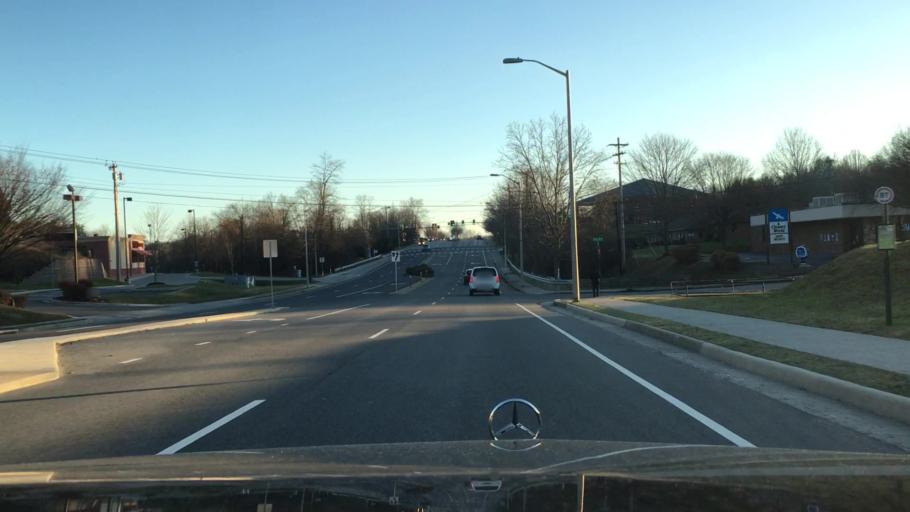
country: US
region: Virginia
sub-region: Montgomery County
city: Blacksburg
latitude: 37.2112
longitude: -80.3998
